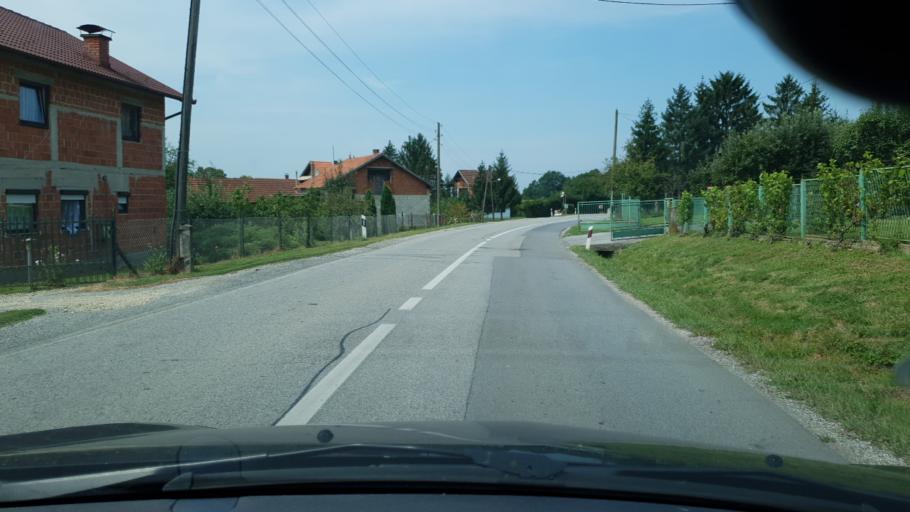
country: HR
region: Krapinsko-Zagorska
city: Zlatar
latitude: 46.0557
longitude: 16.0629
